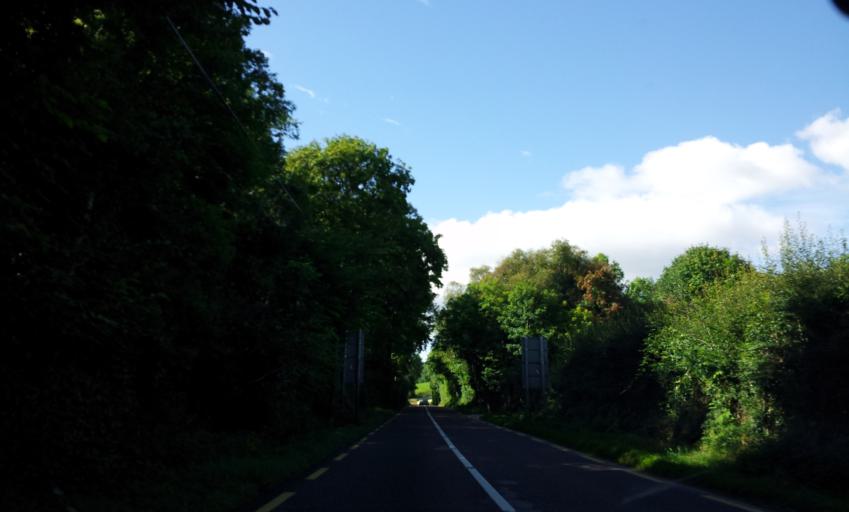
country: IE
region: Munster
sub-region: County Cork
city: Millstreet
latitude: 51.9479
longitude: -9.1786
